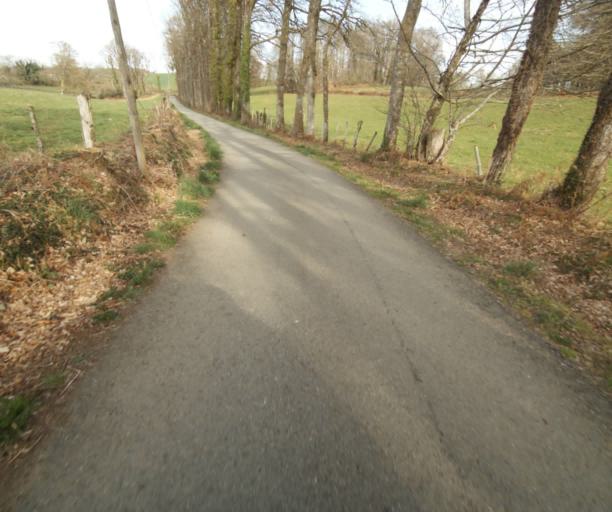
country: FR
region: Limousin
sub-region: Departement de la Correze
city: Chamboulive
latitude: 45.4276
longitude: 1.7508
